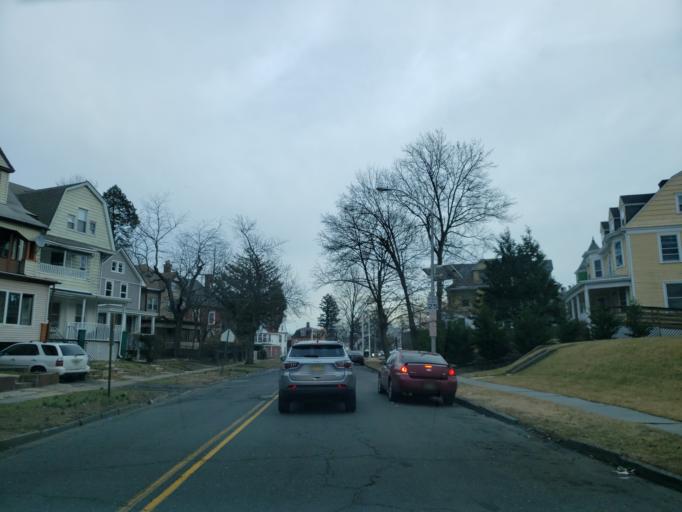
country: US
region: New Jersey
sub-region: Essex County
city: East Orange
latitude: 40.7773
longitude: -74.2146
